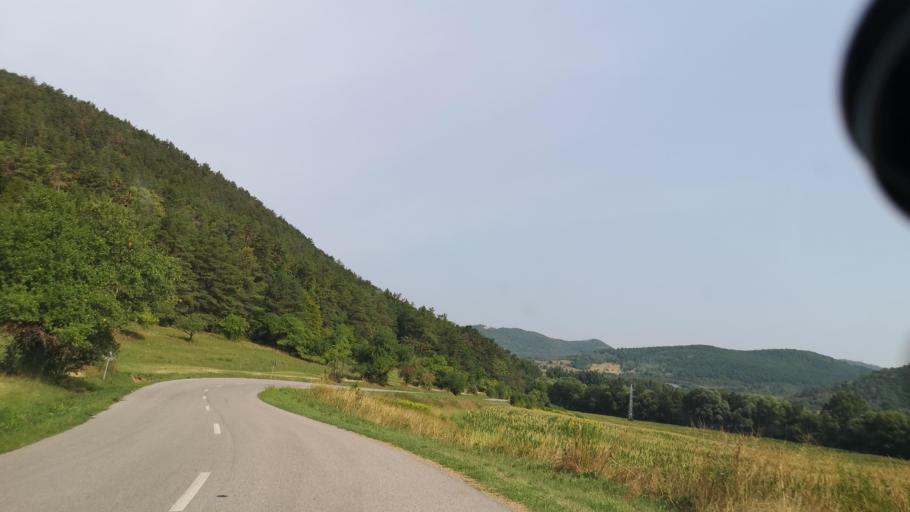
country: SK
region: Banskobystricky
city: Revuca
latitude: 48.6131
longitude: 20.2411
